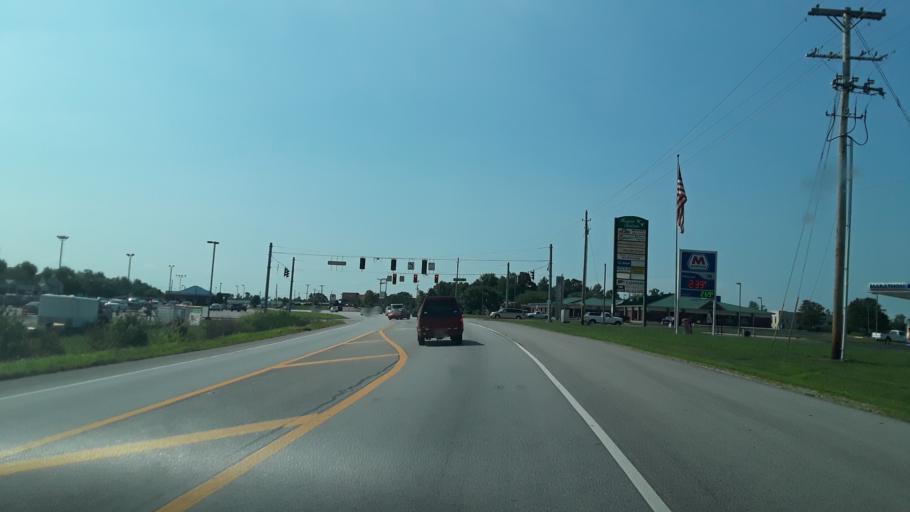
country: US
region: Indiana
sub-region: Clark County
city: Sellersburg
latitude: 38.3837
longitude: -85.7712
